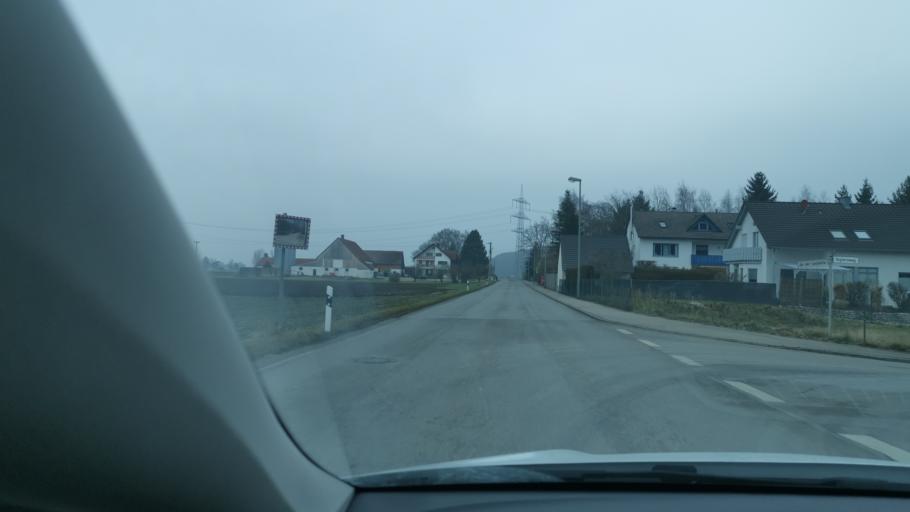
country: DE
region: Bavaria
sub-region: Swabia
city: Rehling
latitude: 48.4969
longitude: 10.9210
